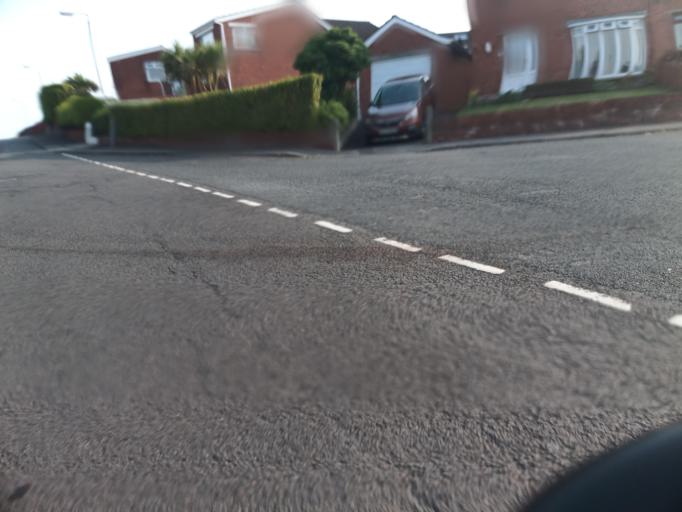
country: GB
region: Northern Ireland
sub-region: Ards District
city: Comber
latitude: 54.5528
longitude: -5.7350
